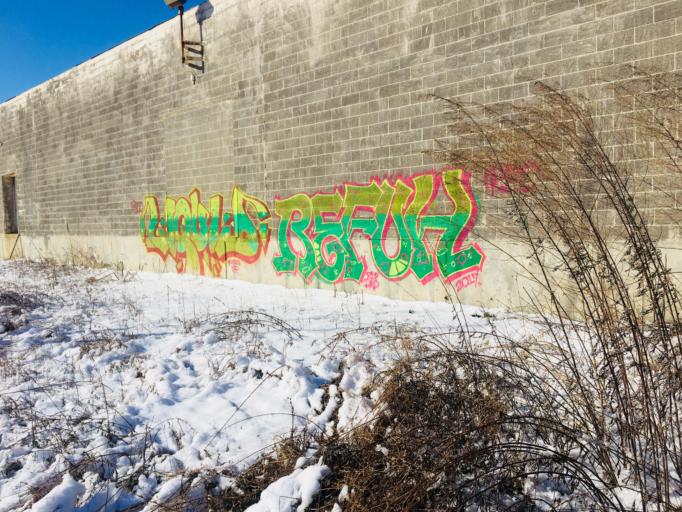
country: US
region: Michigan
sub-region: Wayne County
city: Hamtramck
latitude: 42.4261
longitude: -83.0363
